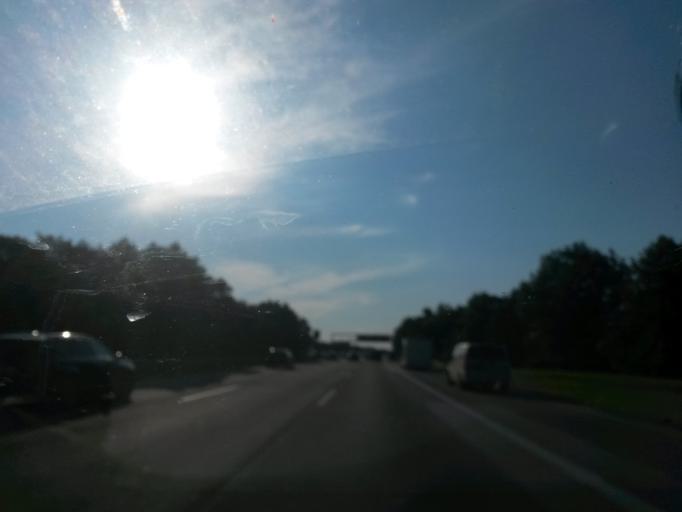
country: DE
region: Bavaria
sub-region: Upper Bavaria
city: Unterfoehring
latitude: 48.1980
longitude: 11.6738
